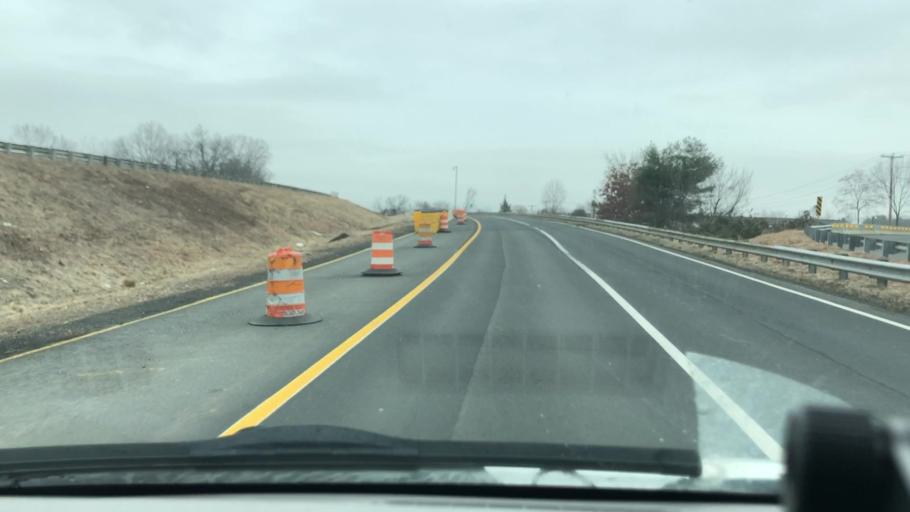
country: US
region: Massachusetts
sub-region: Hampshire County
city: Northampton
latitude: 42.3416
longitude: -72.6403
